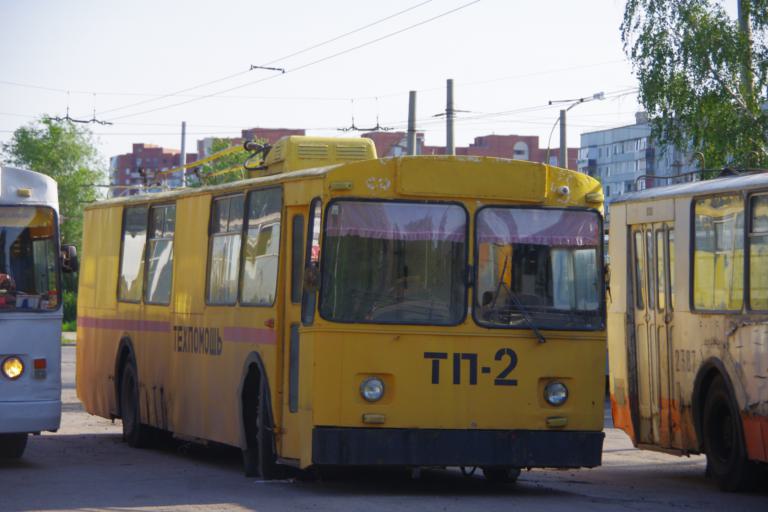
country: RU
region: Samara
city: Tol'yatti
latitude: 53.5062
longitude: 49.2929
